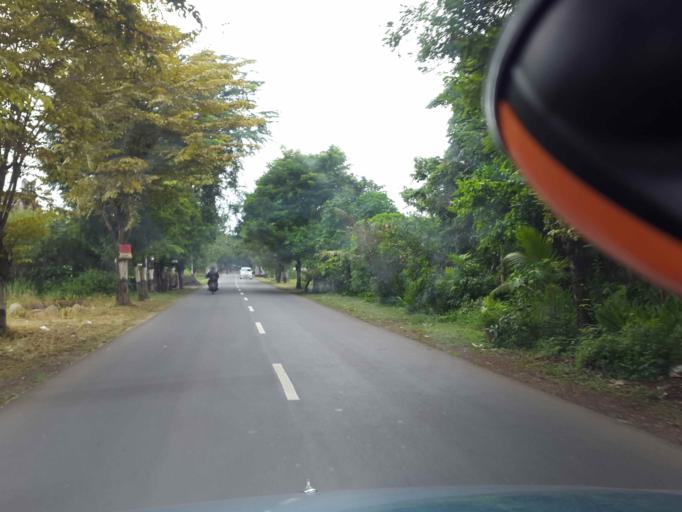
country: ID
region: Central Java
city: Wonopringgo
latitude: -7.0075
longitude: 109.6342
